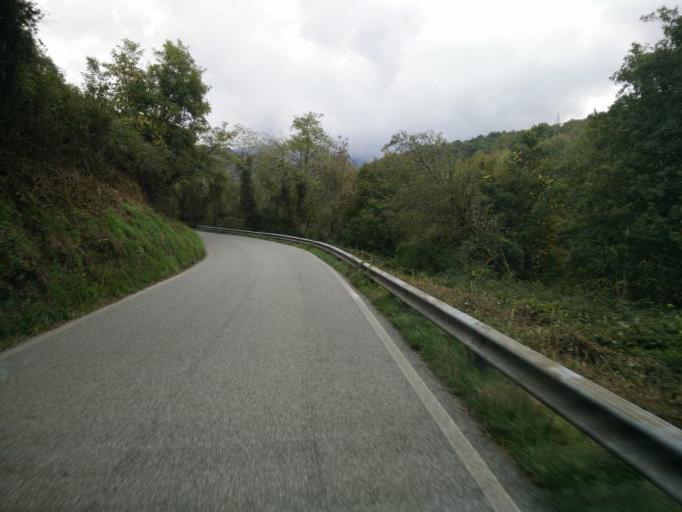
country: IT
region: Tuscany
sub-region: Provincia di Massa-Carrara
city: Casola in Lunigiana
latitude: 44.1898
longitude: 10.1344
